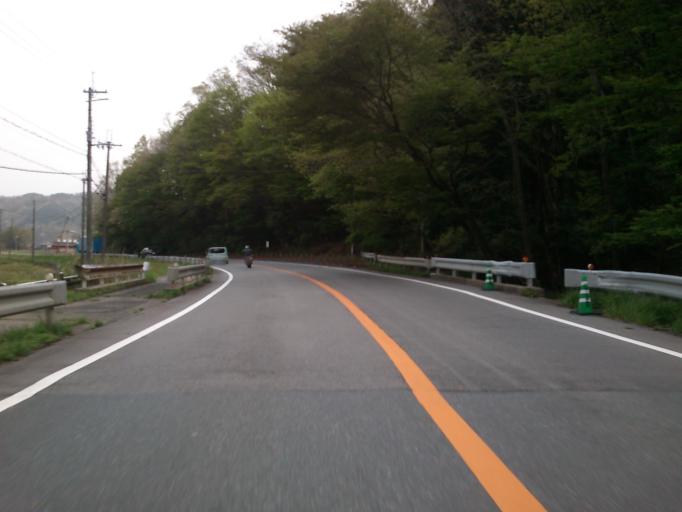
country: JP
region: Hyogo
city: Sasayama
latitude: 35.1303
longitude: 135.3339
